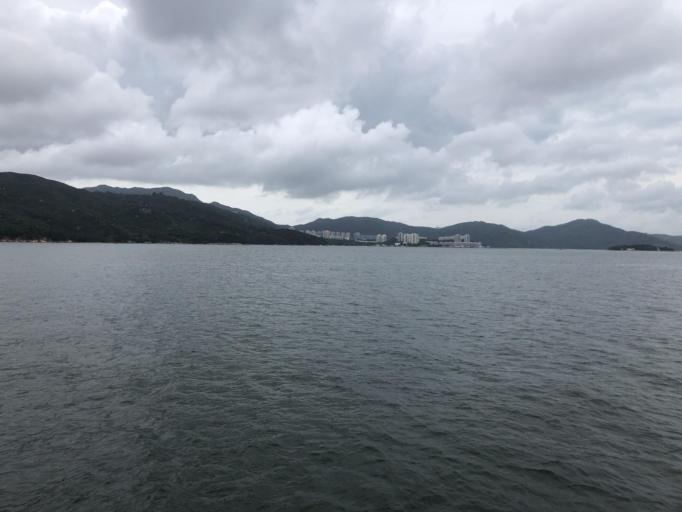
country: HK
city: Yung Shue Wan
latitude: 22.2679
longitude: 114.0320
